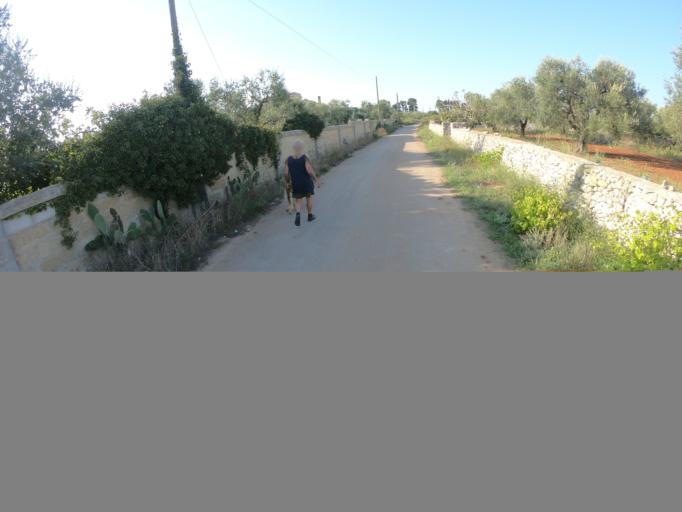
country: IT
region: Apulia
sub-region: Provincia di Lecce
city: Castrignano del Capo
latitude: 39.8368
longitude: 18.3551
